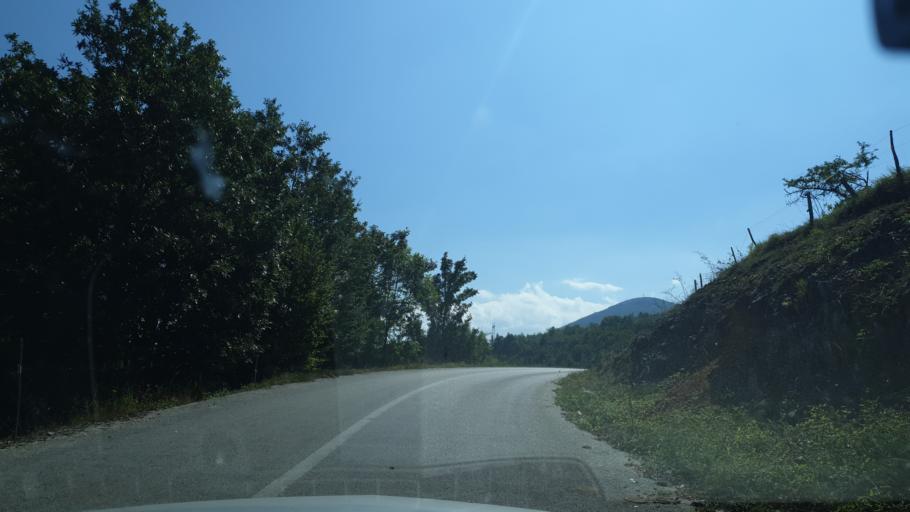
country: RS
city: Zlatibor
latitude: 43.6633
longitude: 19.8279
